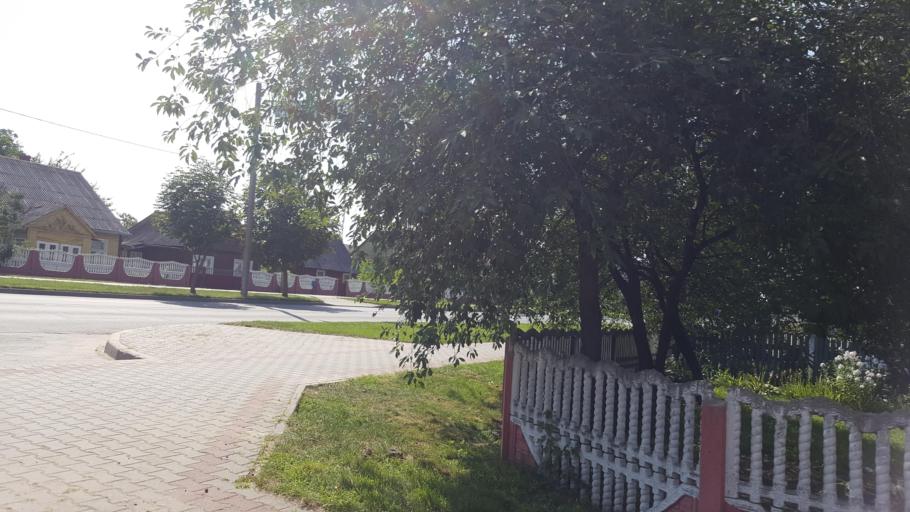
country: BY
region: Brest
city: Zhabinka
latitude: 52.1963
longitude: 24.0132
